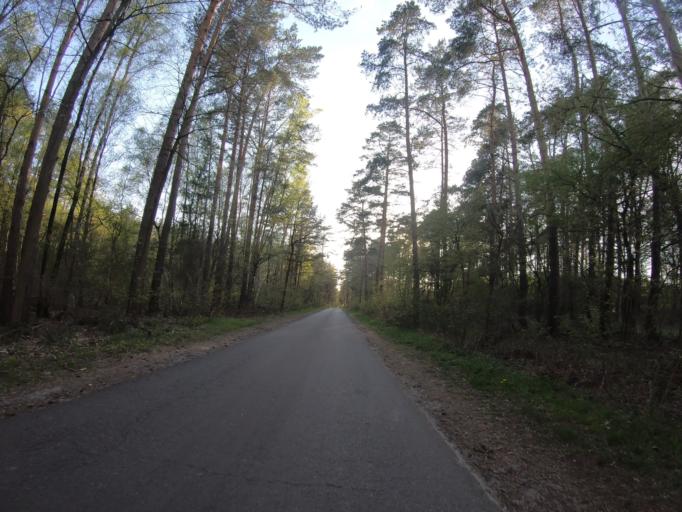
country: DE
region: Lower Saxony
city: Sassenburg
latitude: 52.4810
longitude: 10.6257
